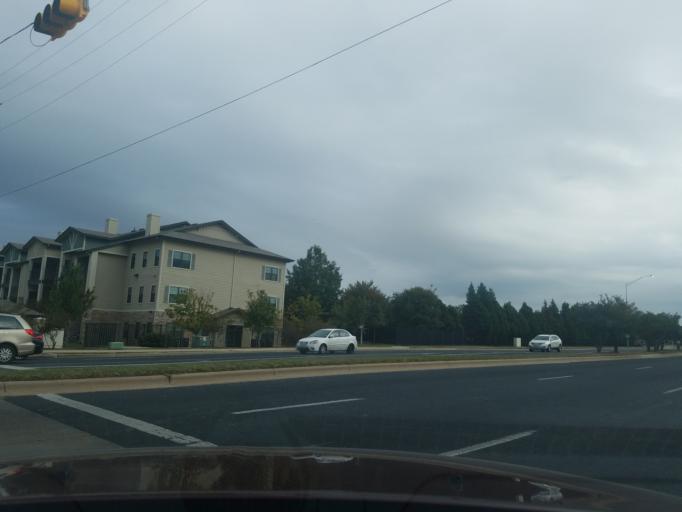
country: US
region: Texas
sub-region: Williamson County
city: Anderson Mill
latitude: 30.4768
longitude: -97.8070
